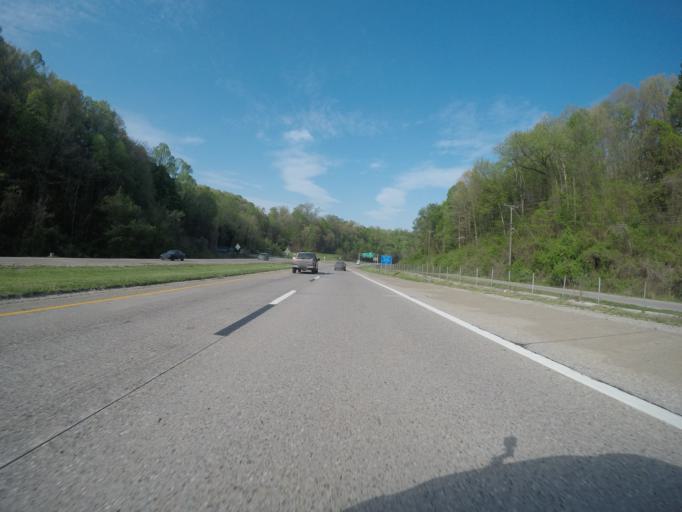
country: US
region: West Virginia
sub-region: Kanawha County
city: South Charleston
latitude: 38.3395
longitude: -81.6892
